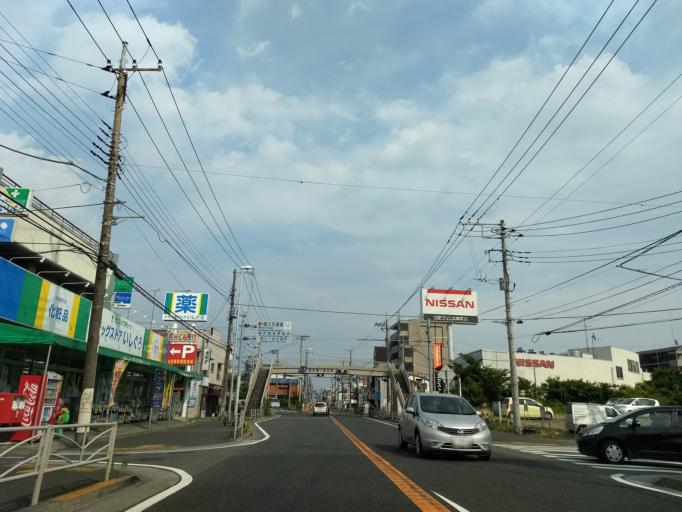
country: JP
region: Kanagawa
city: Minami-rinkan
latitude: 35.4795
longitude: 139.5370
